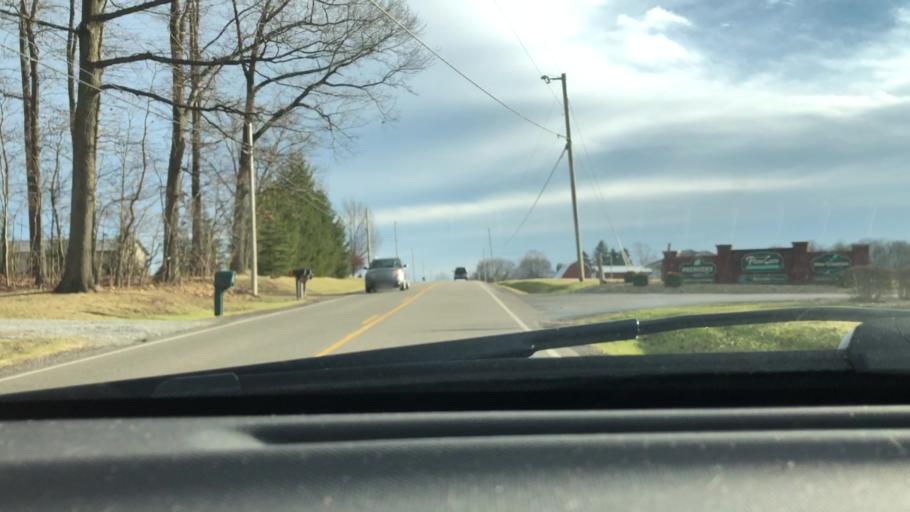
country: US
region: Ohio
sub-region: Wayne County
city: Dalton
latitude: 40.7890
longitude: -81.7454
